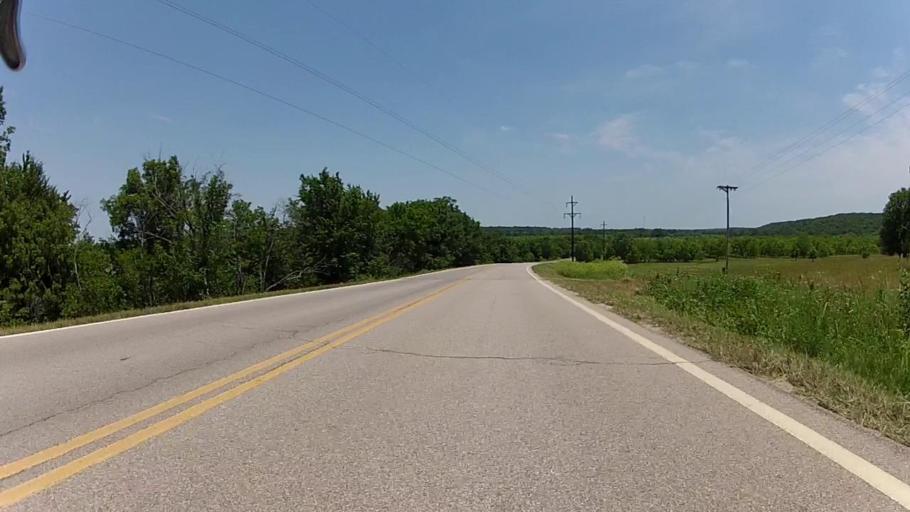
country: US
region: Kansas
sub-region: Chautauqua County
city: Sedan
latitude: 37.1199
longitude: -96.2332
